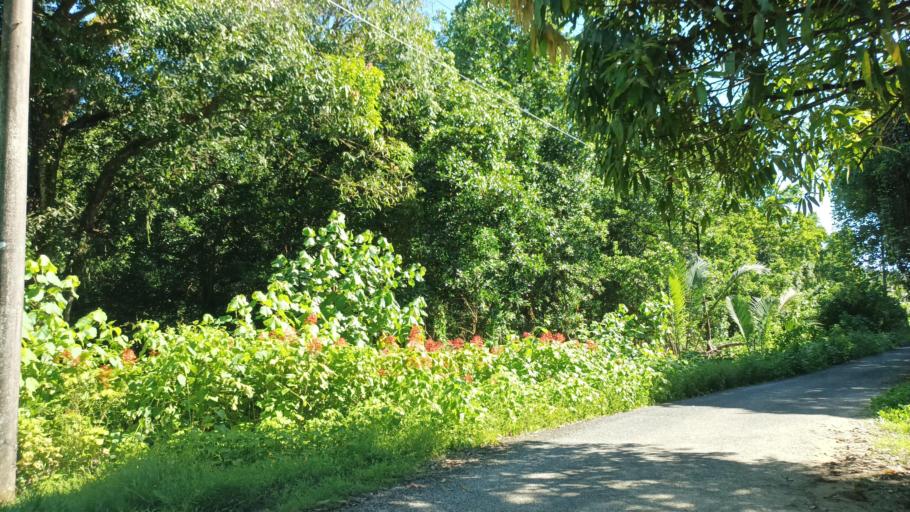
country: FM
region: Pohnpei
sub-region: Madolenihm Municipality
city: Madolenihm Municipality Government
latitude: 6.8463
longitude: 158.3161
